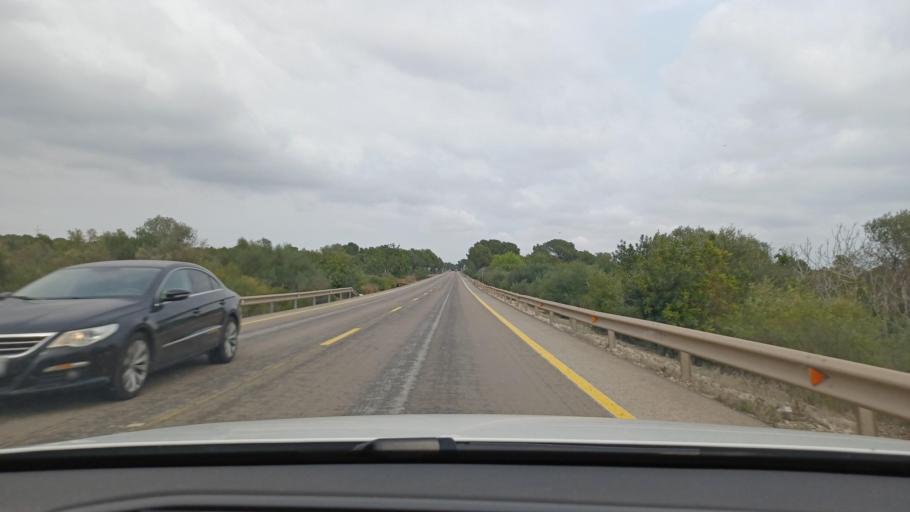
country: ES
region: Catalonia
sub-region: Provincia de Tarragona
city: Sant Carles de la Rapita
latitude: 40.6001
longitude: 0.5618
